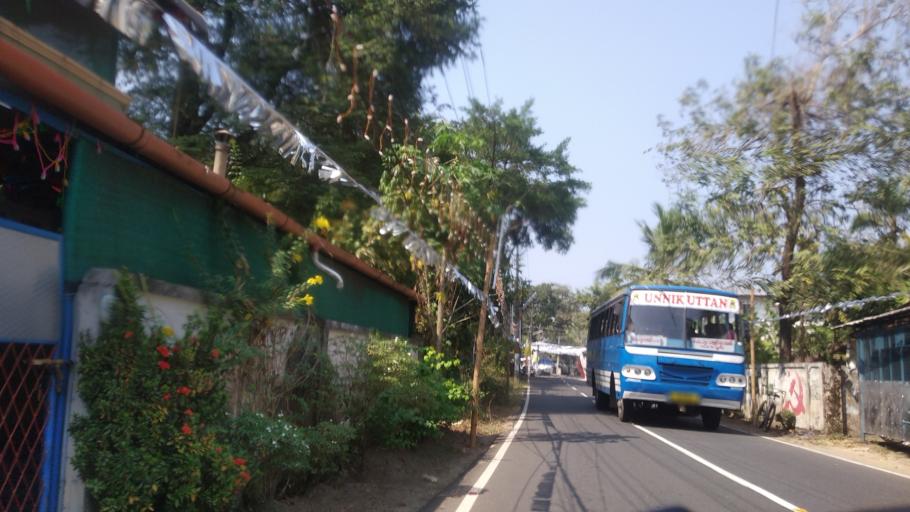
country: IN
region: Kerala
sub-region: Ernakulam
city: Elur
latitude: 10.1241
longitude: 76.2386
